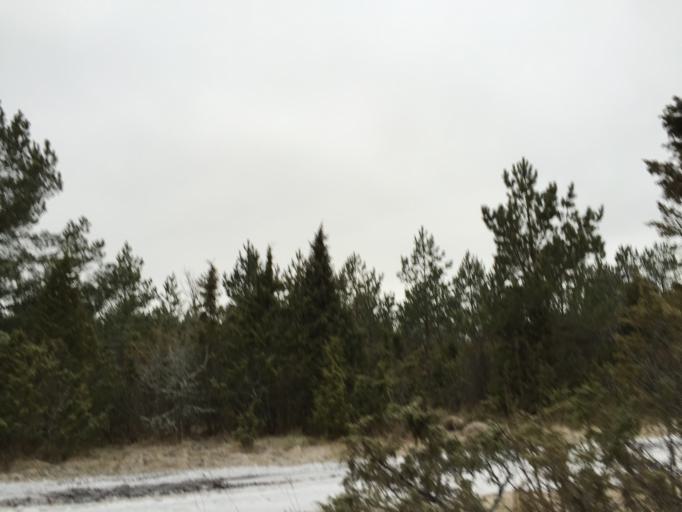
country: EE
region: Saare
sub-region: Orissaare vald
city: Orissaare
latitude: 58.6064
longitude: 23.1151
